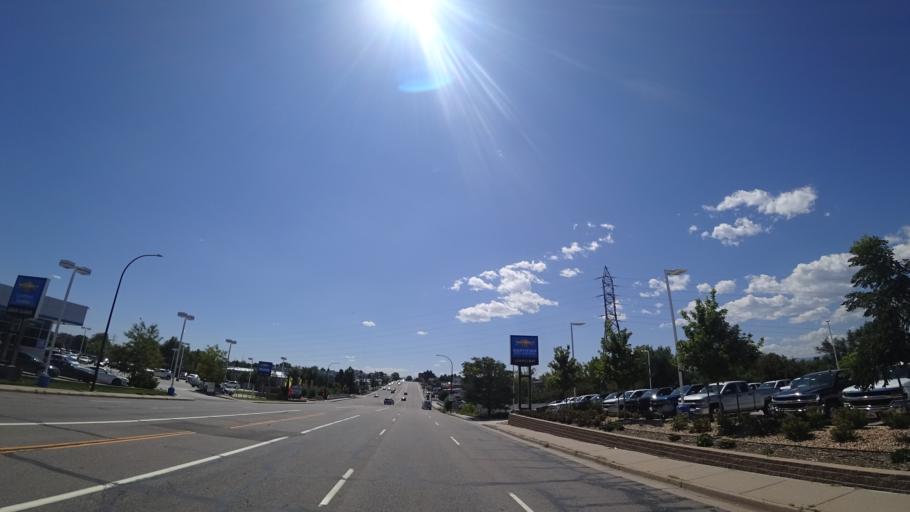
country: US
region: Colorado
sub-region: Arapahoe County
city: Englewood
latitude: 39.6214
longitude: -104.9881
